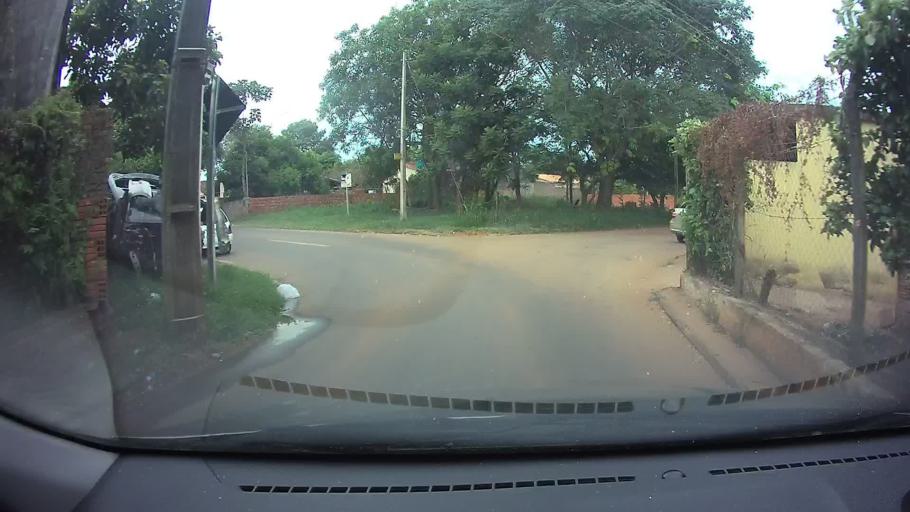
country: PY
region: Central
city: San Lorenzo
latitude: -25.2791
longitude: -57.4791
